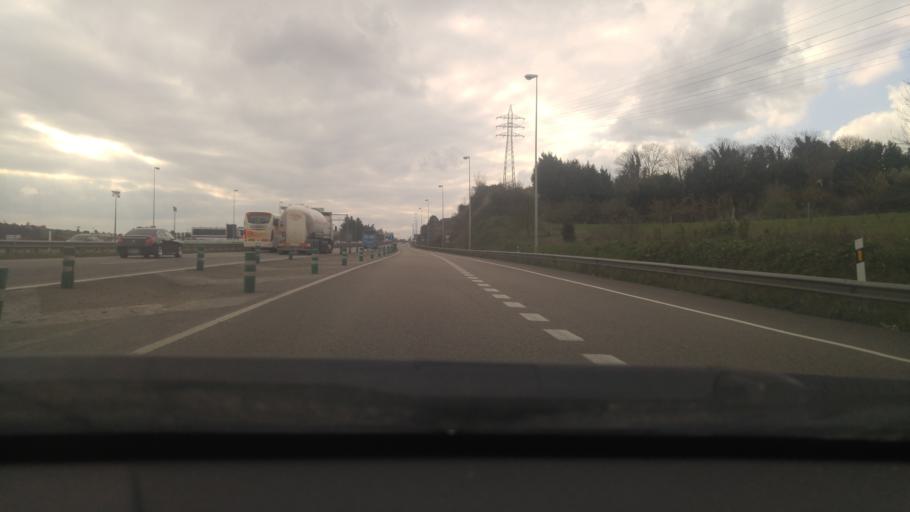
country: ES
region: Asturias
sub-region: Province of Asturias
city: Gijon
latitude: 43.5147
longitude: -5.6593
